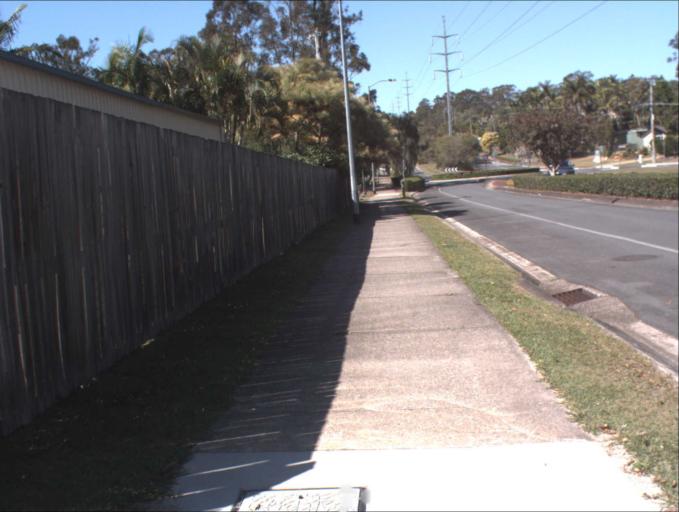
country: AU
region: Queensland
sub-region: Logan
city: Springwood
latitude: -27.6121
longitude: 153.1430
